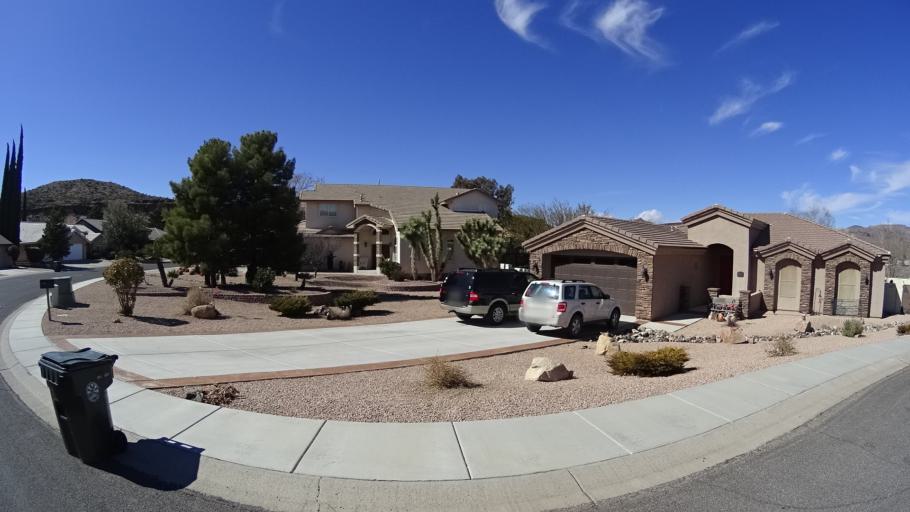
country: US
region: Arizona
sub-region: Mohave County
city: Kingman
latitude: 35.2097
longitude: -114.0469
